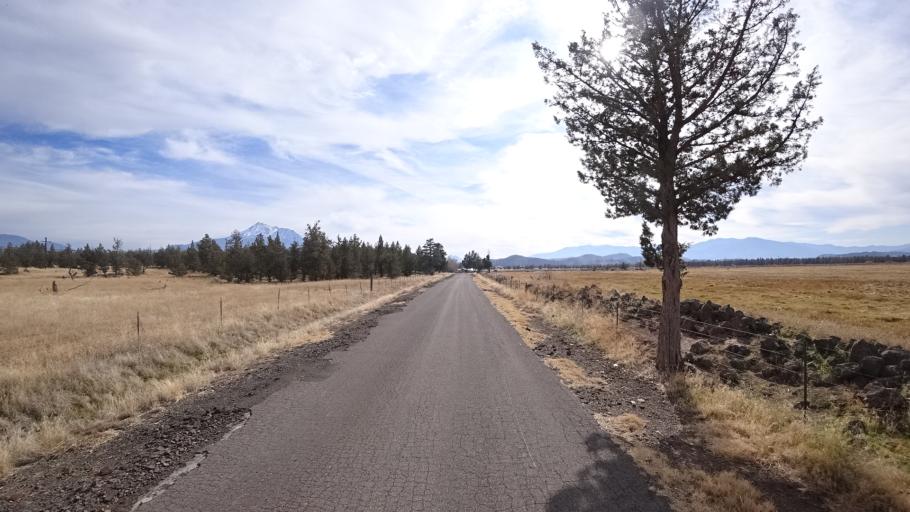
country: US
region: California
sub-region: Siskiyou County
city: Montague
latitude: 41.6030
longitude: -122.4041
